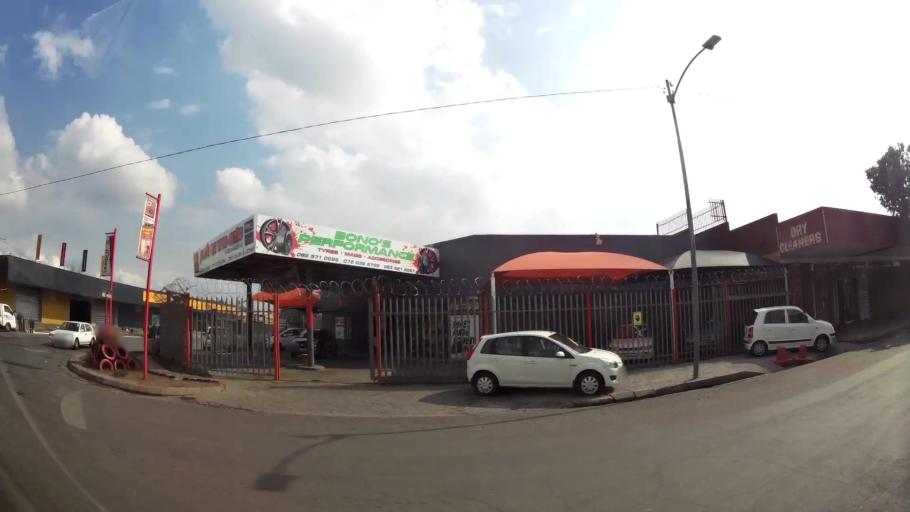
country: ZA
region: Gauteng
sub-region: Sedibeng District Municipality
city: Vereeniging
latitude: -26.6847
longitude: 27.9315
